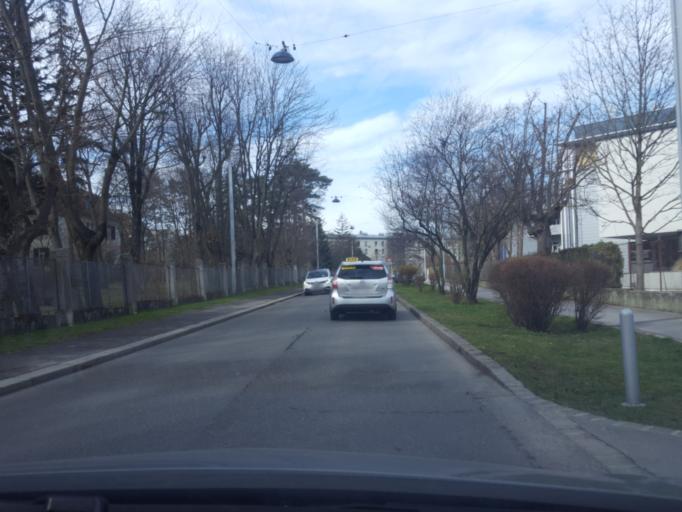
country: AT
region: Lower Austria
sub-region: Politischer Bezirk Modling
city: Perchtoldsdorf
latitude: 48.1627
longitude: 16.2837
